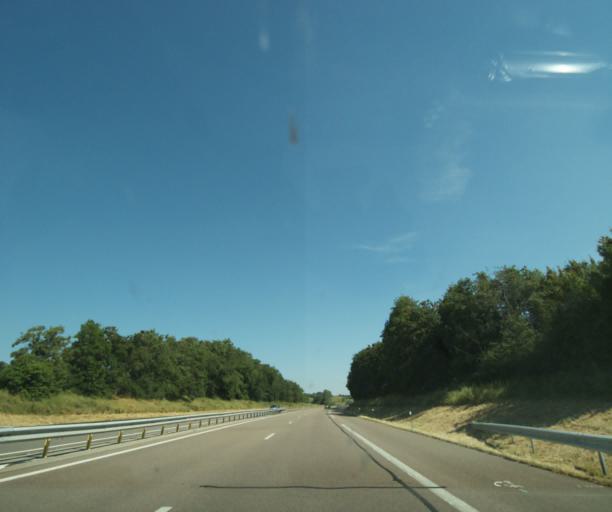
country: FR
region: Lorraine
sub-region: Departement des Vosges
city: Chatenois
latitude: 48.3880
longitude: 5.8804
